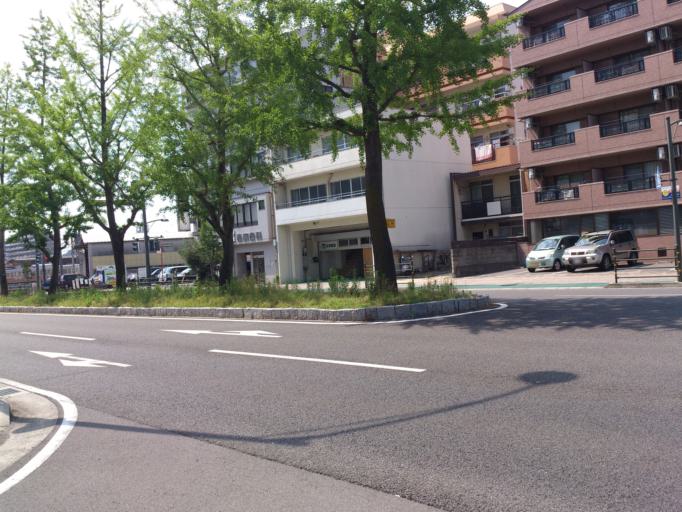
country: JP
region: Ehime
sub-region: Shikoku-chuo Shi
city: Matsuyama
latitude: 33.8476
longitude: 132.7565
